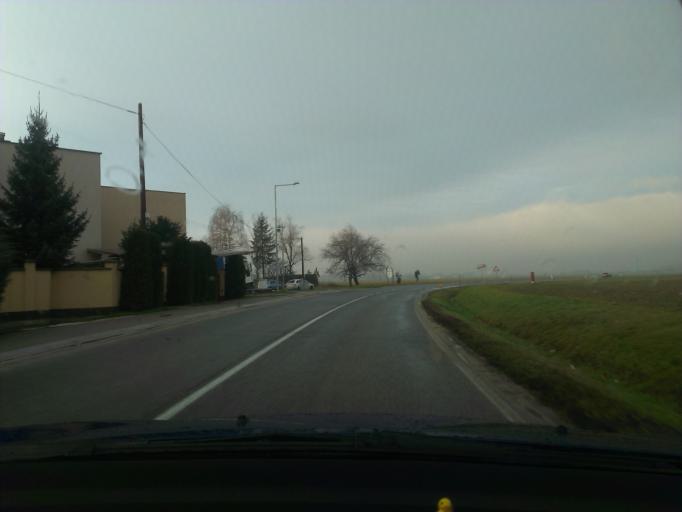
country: SK
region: Trnavsky
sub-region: Okres Trnava
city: Piestany
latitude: 48.6088
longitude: 17.8651
